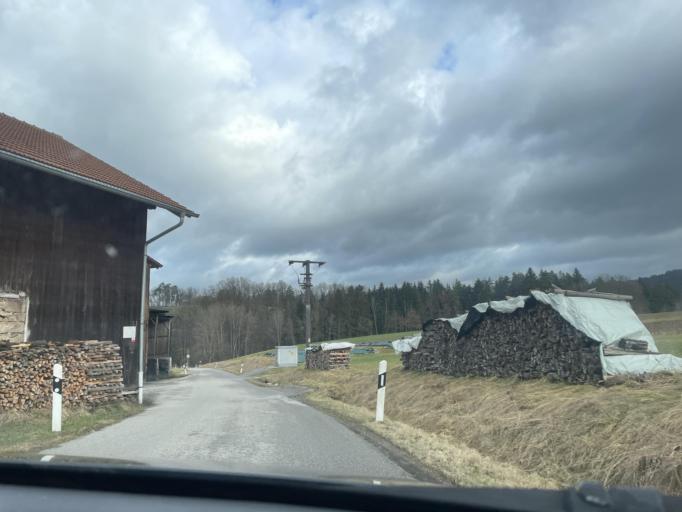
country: DE
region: Bavaria
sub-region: Lower Bavaria
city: Prackenbach
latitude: 49.1311
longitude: 12.8362
